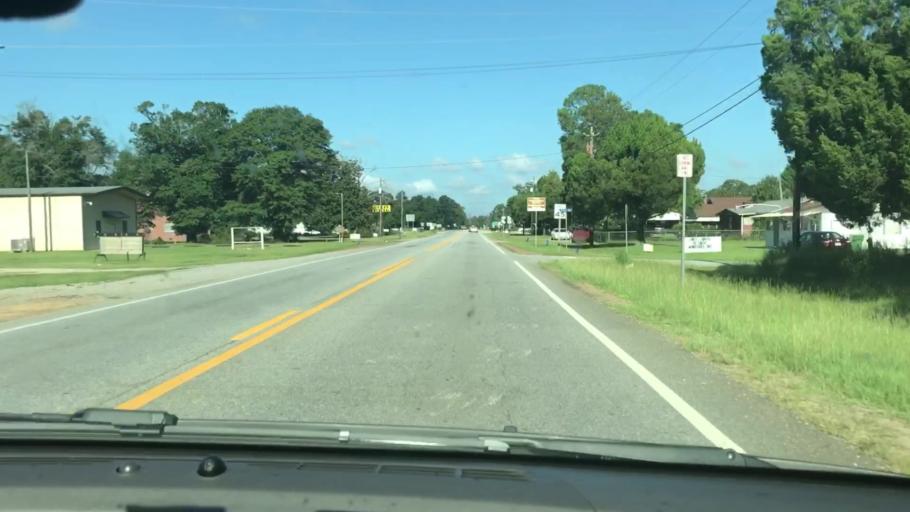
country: US
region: Georgia
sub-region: Quitman County
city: Georgetown
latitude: 31.8821
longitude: -85.0907
